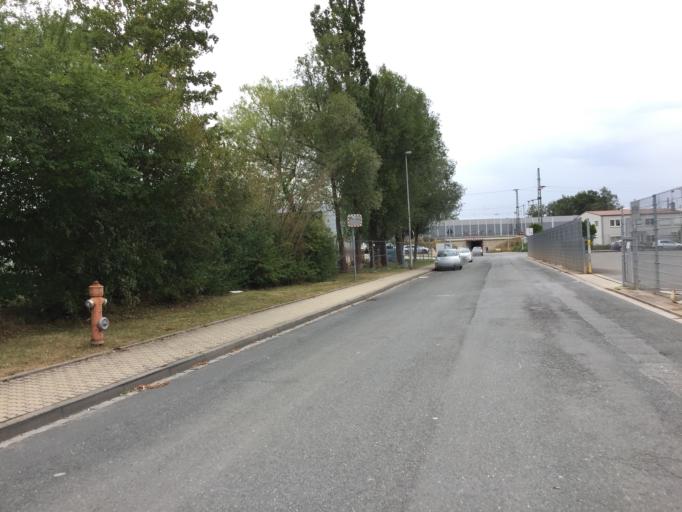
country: DE
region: Bavaria
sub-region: Regierungsbezirk Mittelfranken
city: Erlangen
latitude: 49.5559
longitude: 10.9986
